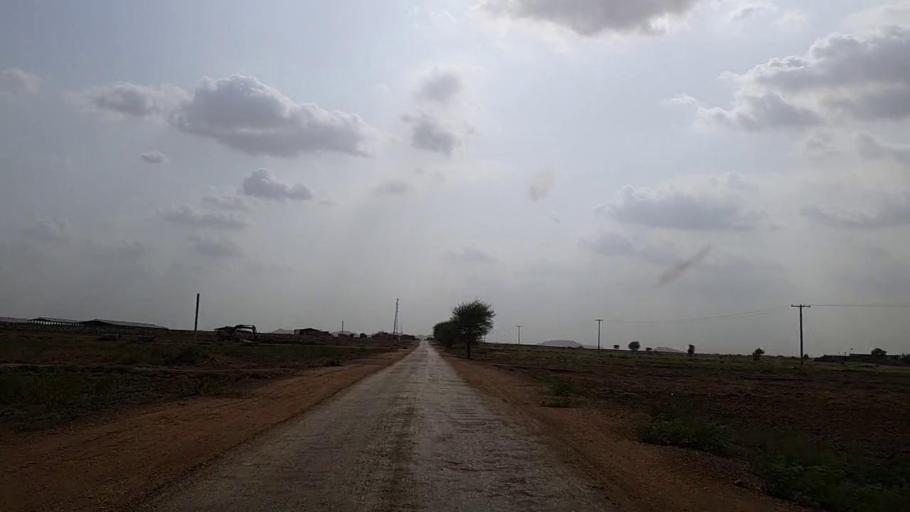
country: PK
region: Sindh
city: Kotri
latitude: 25.2530
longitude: 68.2389
